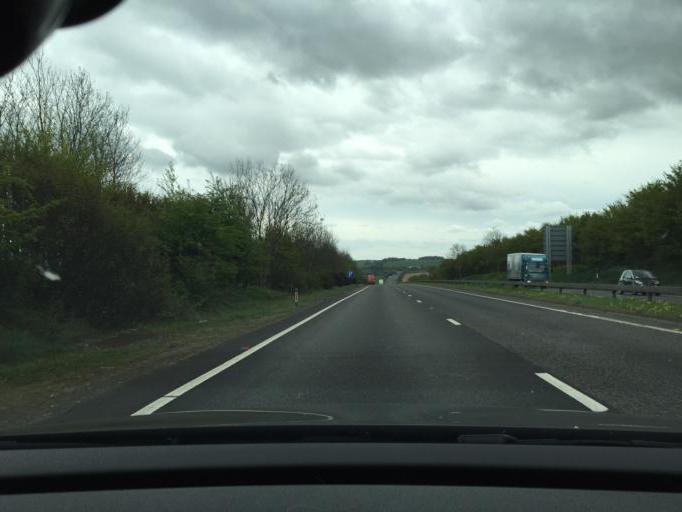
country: GB
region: England
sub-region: Oxfordshire
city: Harwell
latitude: 51.5446
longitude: -1.2936
